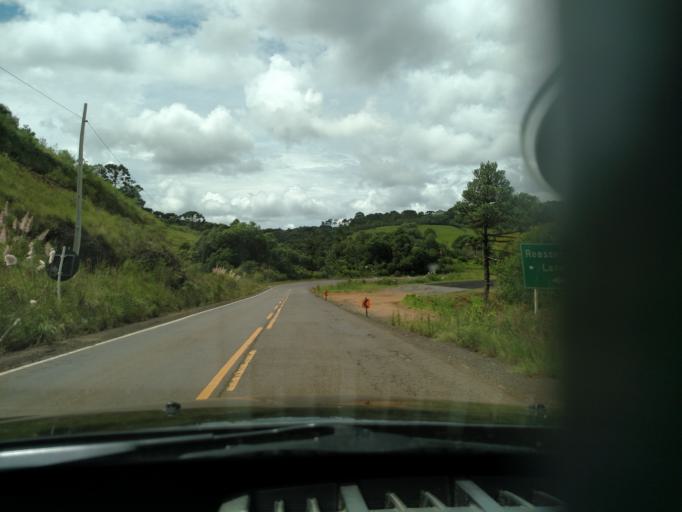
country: BR
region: Santa Catarina
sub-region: Lages
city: Lages
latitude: -27.9214
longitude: -50.6277
